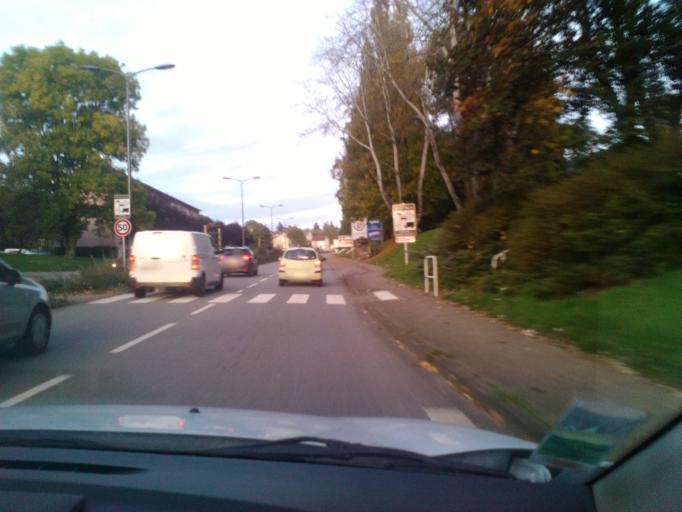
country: FR
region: Lorraine
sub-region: Departement des Vosges
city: Epinal
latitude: 48.1939
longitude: 6.4556
